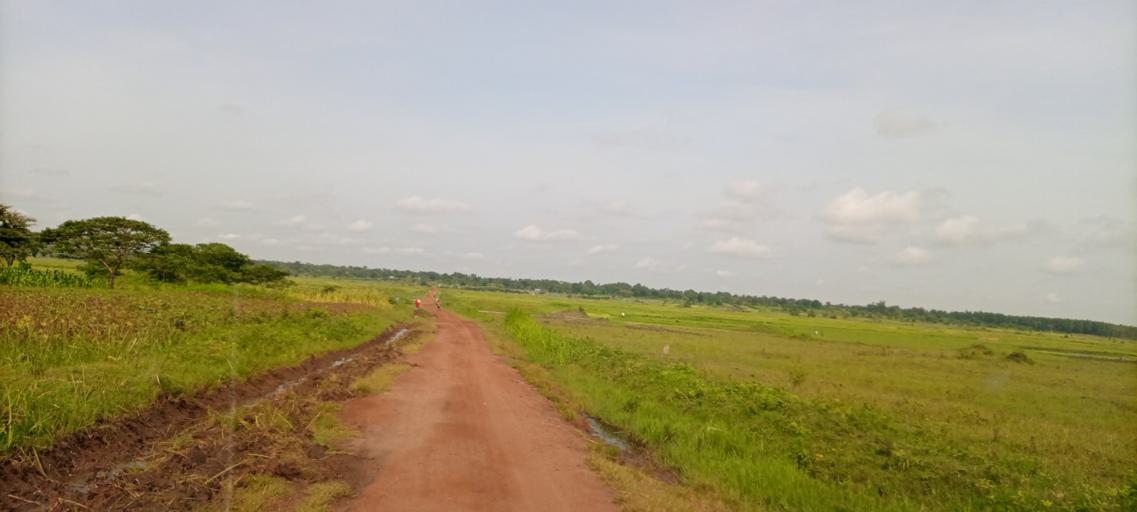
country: UG
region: Eastern Region
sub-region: Kibuku District
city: Kibuku
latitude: 1.1019
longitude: 33.7779
